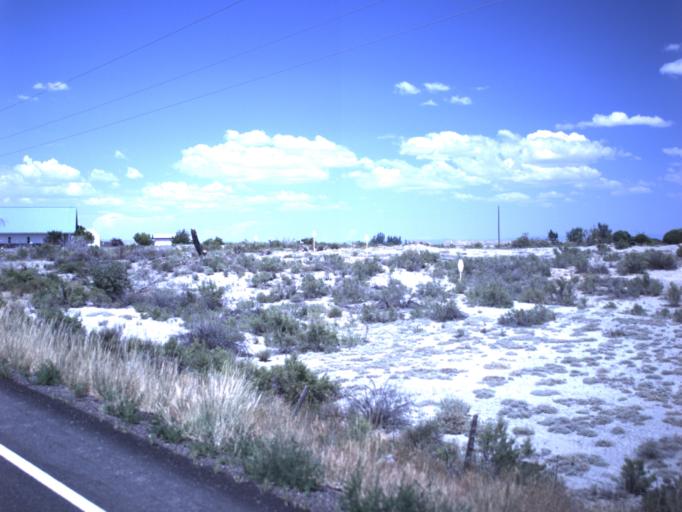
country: US
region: Utah
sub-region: Emery County
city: Huntington
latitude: 39.3167
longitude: -110.9644
